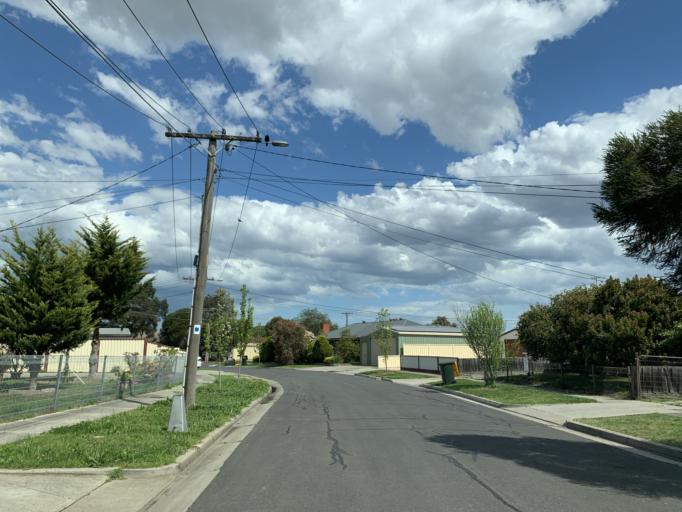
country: AU
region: Victoria
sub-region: Brimbank
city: Albion
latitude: -37.7574
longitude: 144.8283
